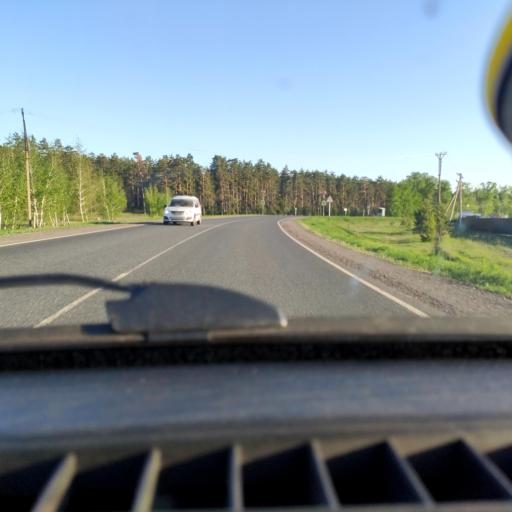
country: RU
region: Samara
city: Povolzhskiy
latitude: 53.6319
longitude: 49.6592
